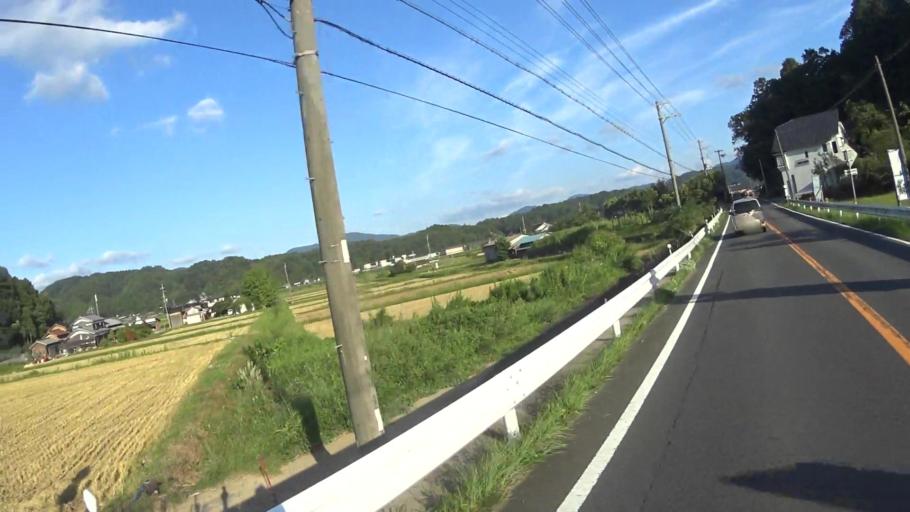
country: JP
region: Hyogo
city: Toyooka
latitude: 35.5932
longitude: 134.9207
